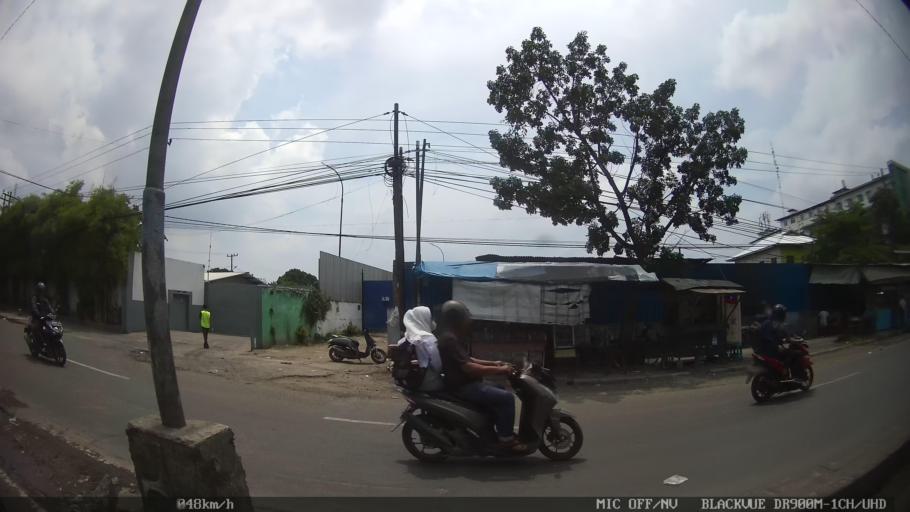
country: ID
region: North Sumatra
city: Medan
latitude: 3.6334
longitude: 98.6694
